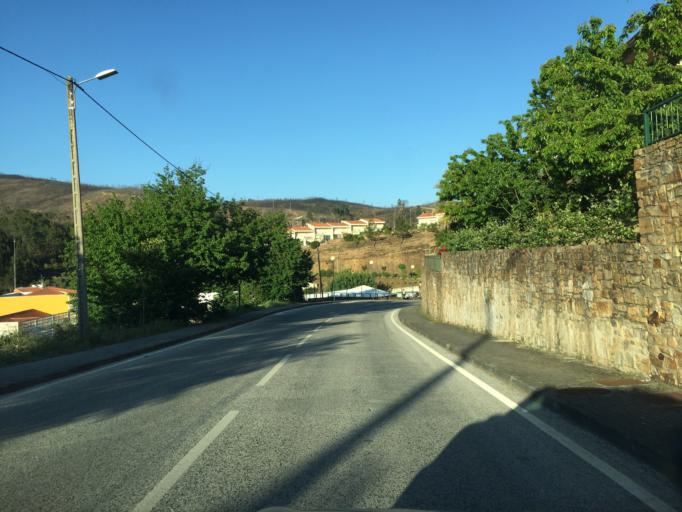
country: PT
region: Coimbra
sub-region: Pampilhosa da Serra
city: Pampilhosa da Serra
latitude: 40.0432
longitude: -7.9518
